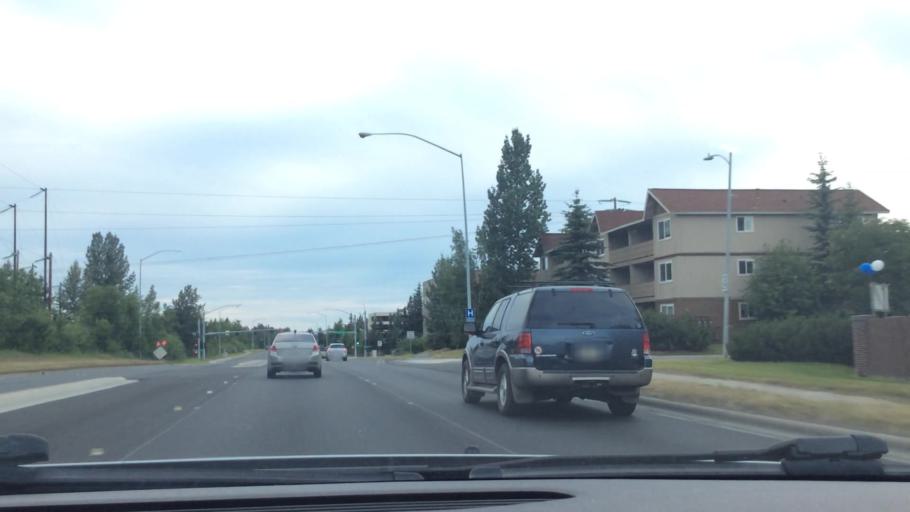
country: US
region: Alaska
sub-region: Anchorage Municipality
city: Anchorage
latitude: 61.1808
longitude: -149.7914
